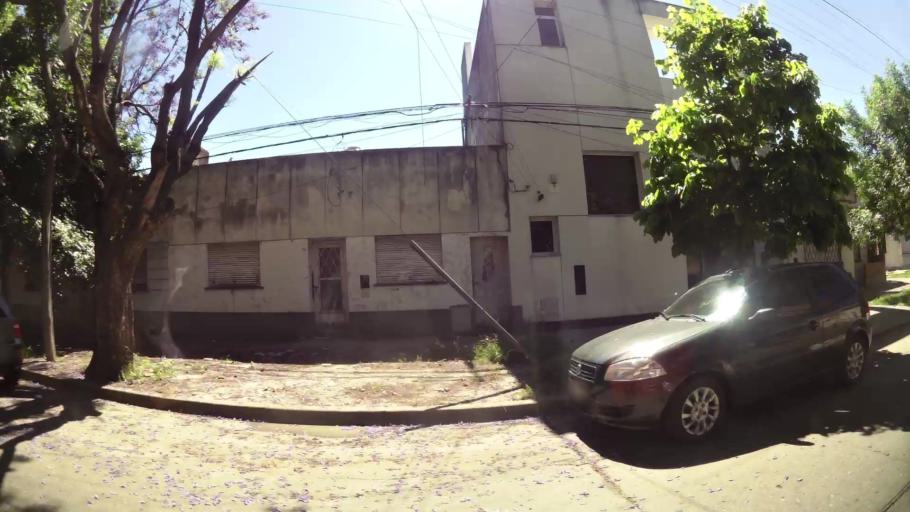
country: AR
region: Santa Fe
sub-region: Departamento de Rosario
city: Rosario
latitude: -32.9360
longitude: -60.6812
